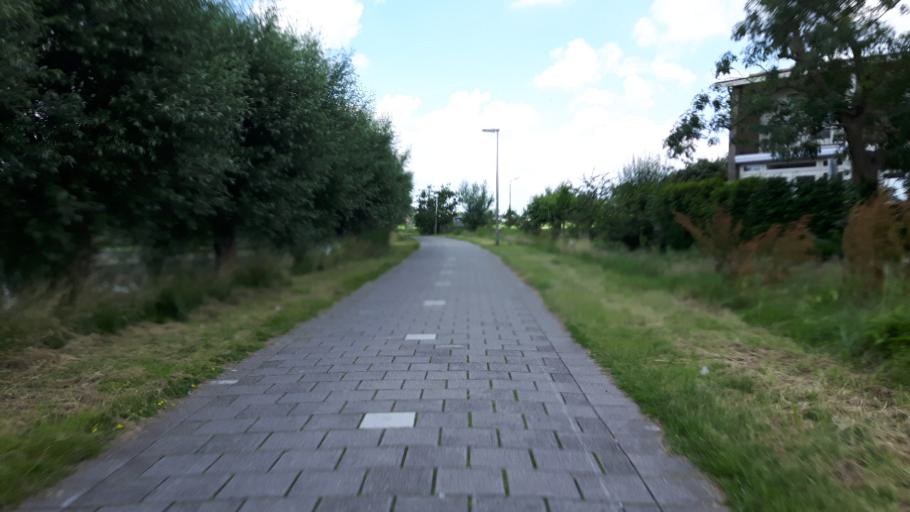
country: NL
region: South Holland
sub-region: Gemeente Gouda
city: Bloemendaal
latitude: 52.0434
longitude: 4.6868
